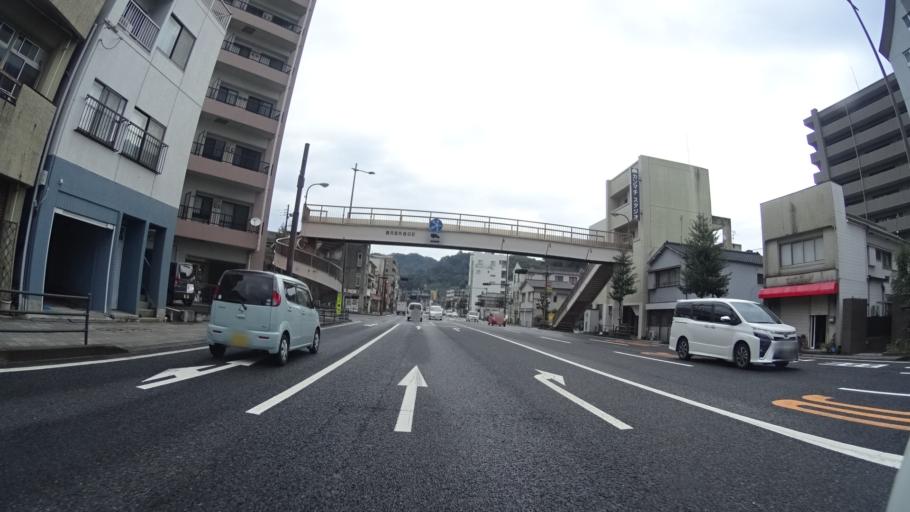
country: JP
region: Kagoshima
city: Kagoshima-shi
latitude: 31.6052
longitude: 130.5660
